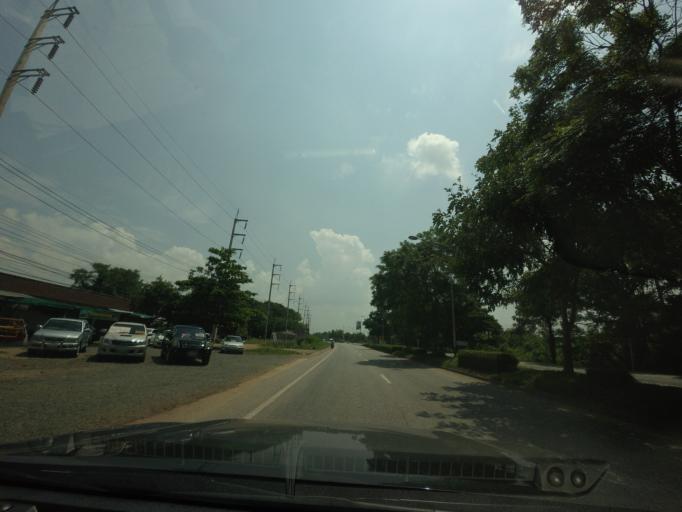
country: TH
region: Uttaradit
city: Uttaradit
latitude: 17.5997
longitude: 100.1256
